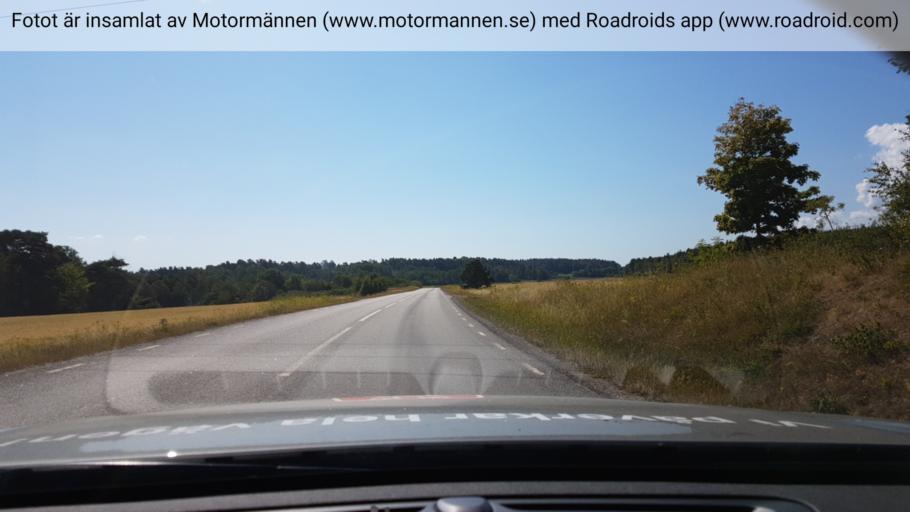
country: SE
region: Stockholm
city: Stenhamra
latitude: 59.3894
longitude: 17.5756
